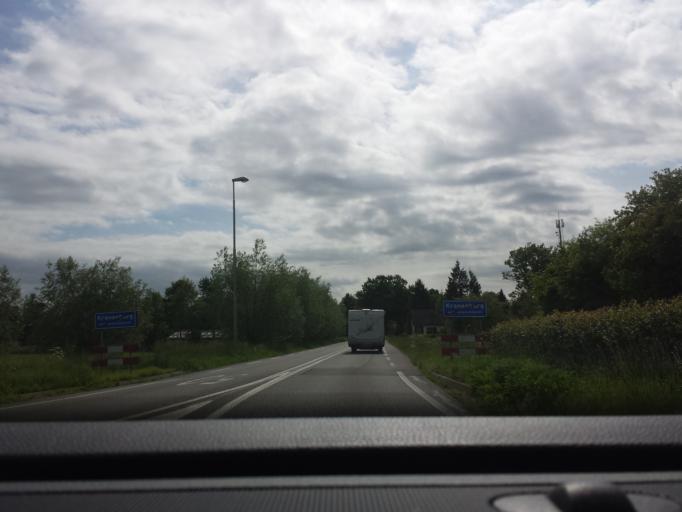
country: NL
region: Gelderland
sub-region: Gemeente Bronckhorst
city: Hengelo
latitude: 52.1008
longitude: 6.3615
